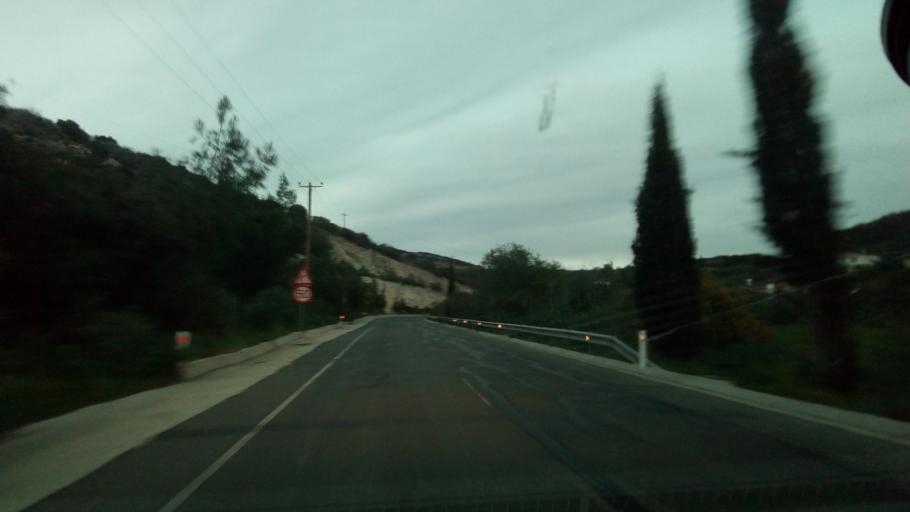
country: CY
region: Pafos
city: Polis
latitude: 34.9866
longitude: 32.4845
